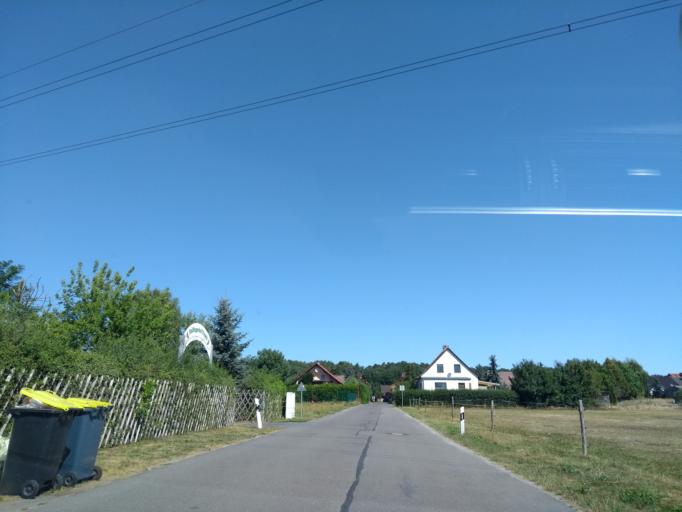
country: DE
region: Brandenburg
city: Lubbenau
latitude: 51.8344
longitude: 13.9501
